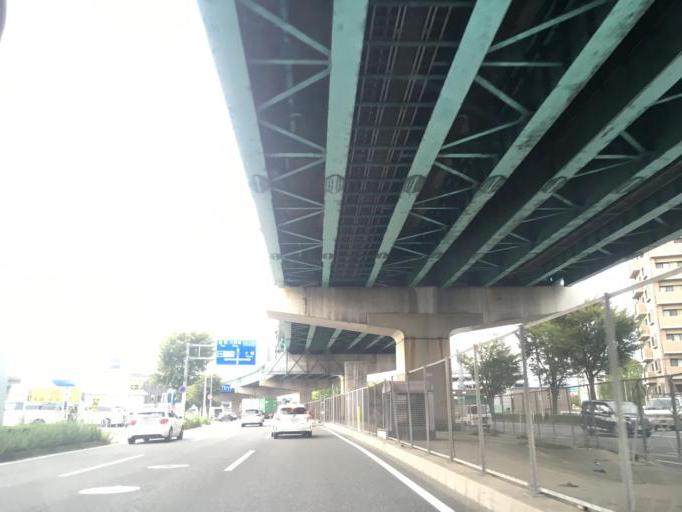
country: JP
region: Fukuoka
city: Fukuoka-shi
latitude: 33.5878
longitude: 130.4386
